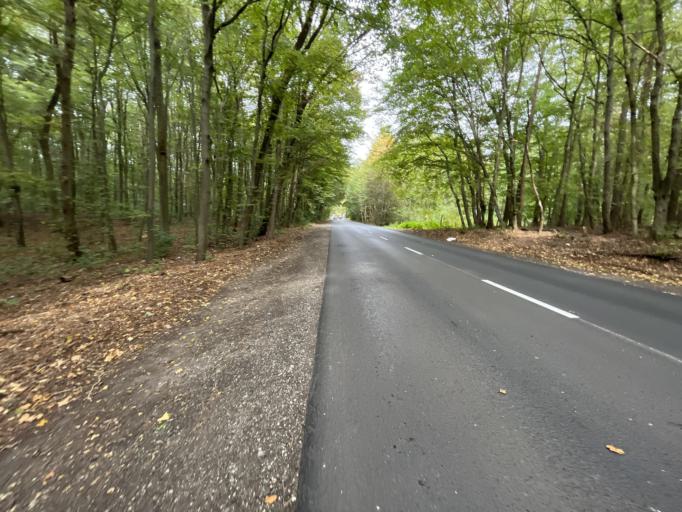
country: PL
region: Greater Poland Voivodeship
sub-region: Powiat poznanski
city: Baranowo
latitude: 52.4624
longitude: 16.7999
